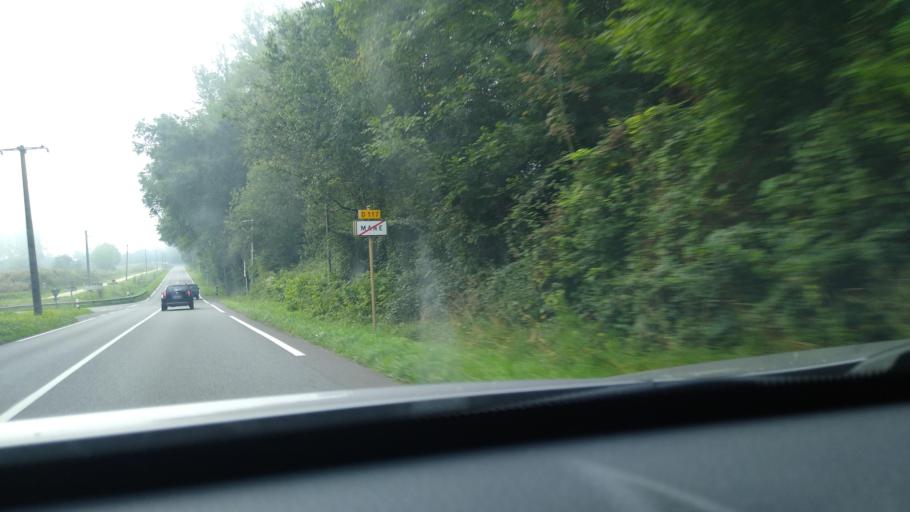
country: FR
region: Midi-Pyrenees
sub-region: Departement de la Haute-Garonne
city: Salies-du-Salat
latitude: 43.0780
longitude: 0.9579
